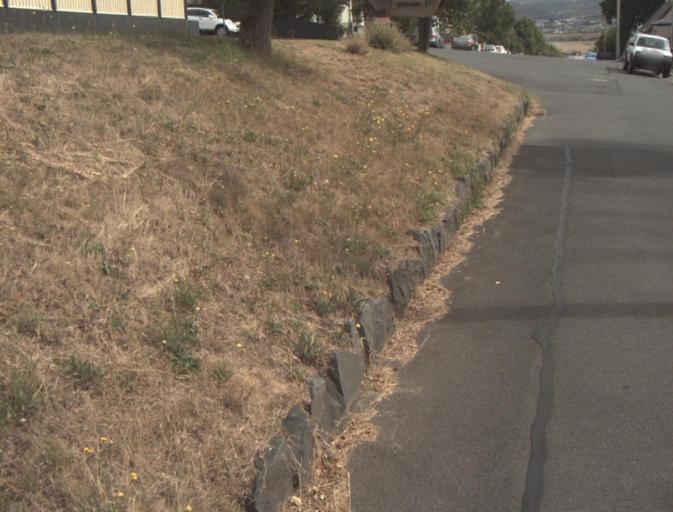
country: AU
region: Tasmania
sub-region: Launceston
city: East Launceston
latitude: -41.4371
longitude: 147.1500
